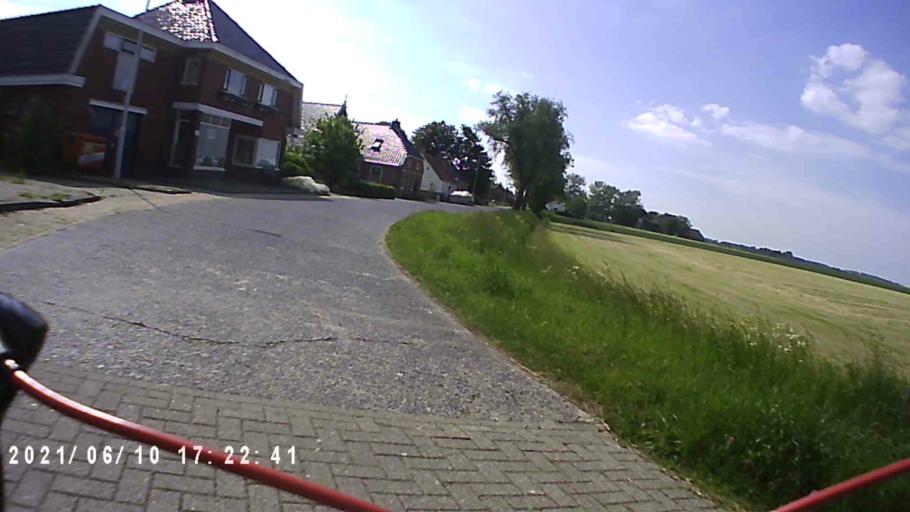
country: NL
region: Friesland
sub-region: Gemeente Kollumerland en Nieuwkruisland
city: Kollum
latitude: 53.2960
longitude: 6.2324
